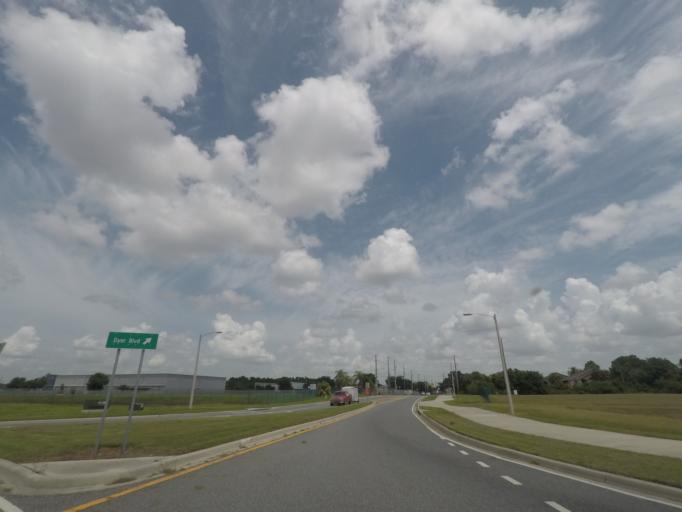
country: US
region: Florida
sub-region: Osceola County
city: Kissimmee
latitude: 28.2963
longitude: -81.4367
